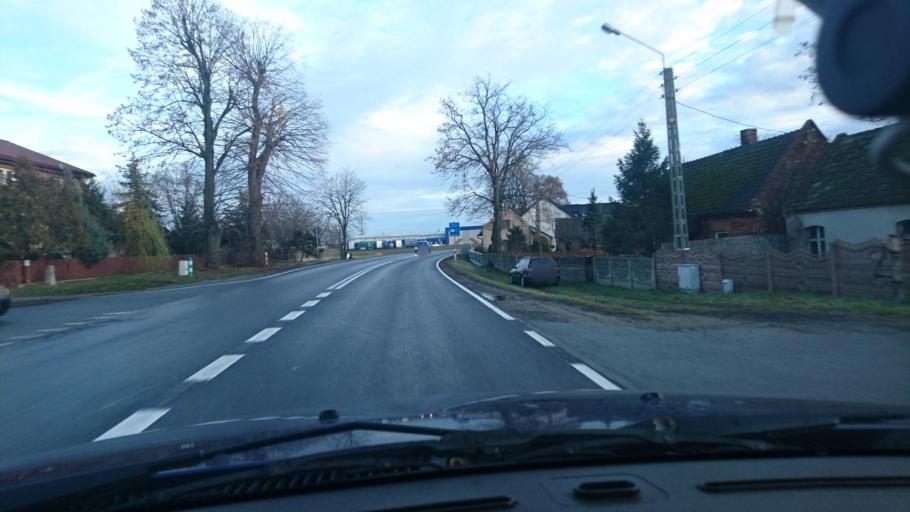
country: PL
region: Greater Poland Voivodeship
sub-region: Powiat kepinski
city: Slupia pod Kepnem
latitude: 51.2304
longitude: 18.0755
